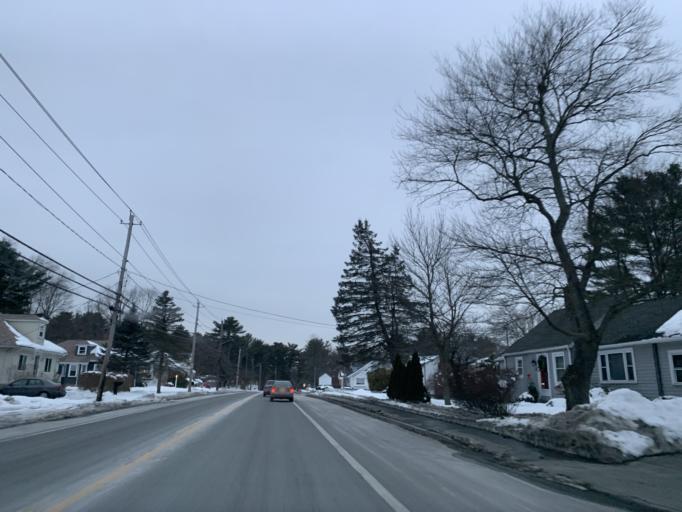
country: US
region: Massachusetts
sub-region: Norfolk County
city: Stoughton
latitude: 42.1143
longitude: -71.0790
